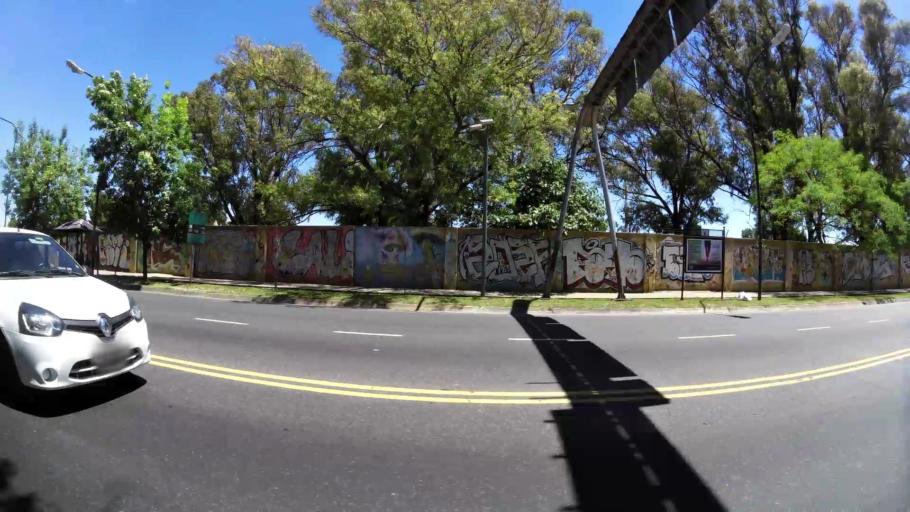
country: AR
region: Buenos Aires
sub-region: Partido de San Isidro
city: San Isidro
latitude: -34.5060
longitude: -58.5637
